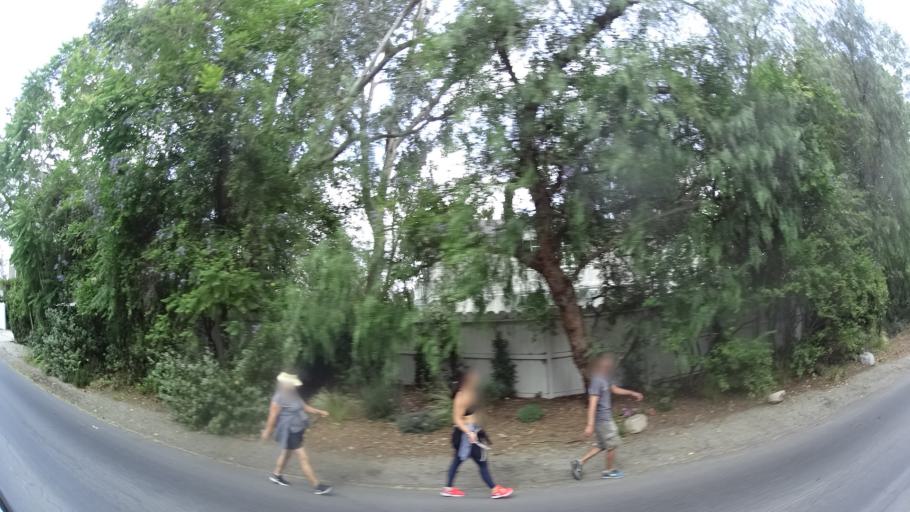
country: US
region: California
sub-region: Los Angeles County
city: Sherman Oaks
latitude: 34.1444
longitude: -118.4276
